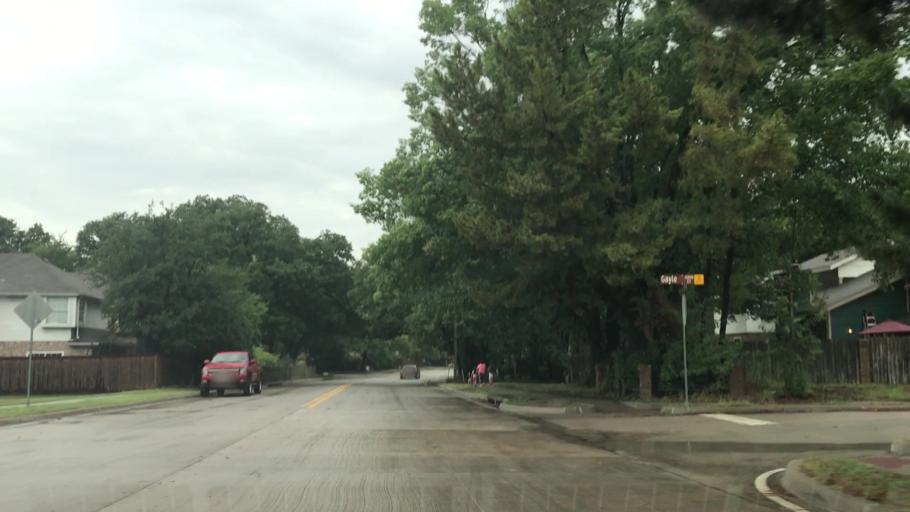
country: US
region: Texas
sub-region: Denton County
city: Highland Village
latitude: 33.0425
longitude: -97.0492
